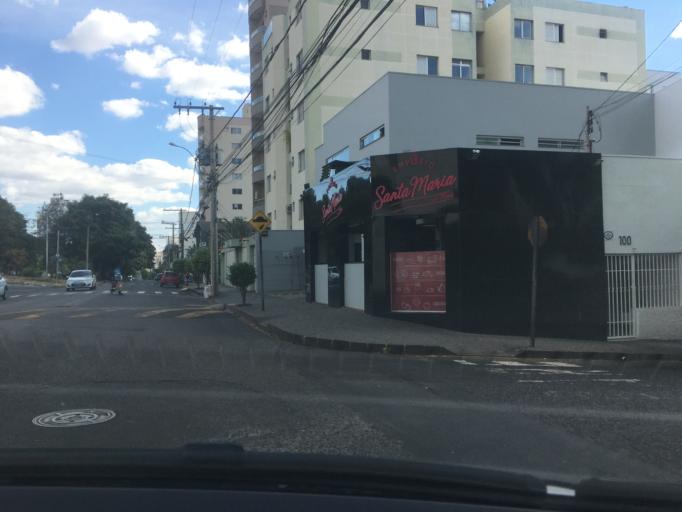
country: BR
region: Minas Gerais
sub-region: Uberlandia
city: Uberlandia
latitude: -18.9144
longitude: -48.2601
